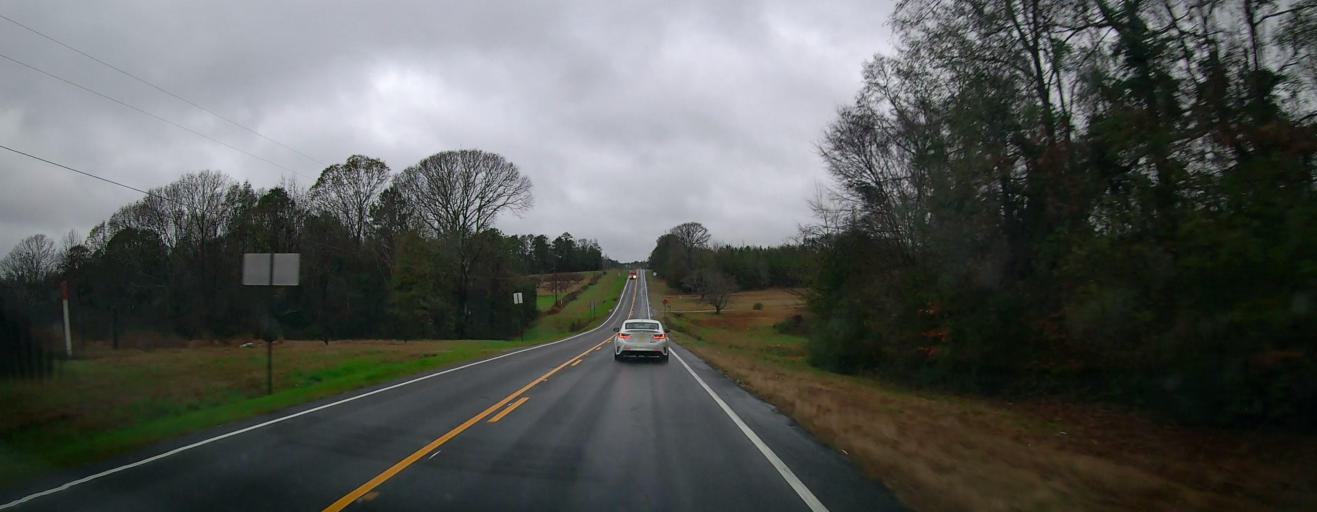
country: US
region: Alabama
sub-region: Chilton County
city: Clanton
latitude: 32.6607
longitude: -86.7715
